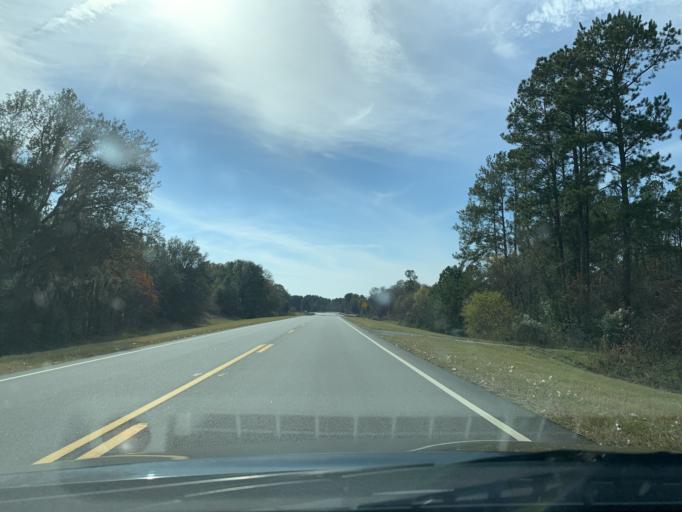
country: US
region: Georgia
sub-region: Turner County
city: Ashburn
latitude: 31.7325
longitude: -83.5778
